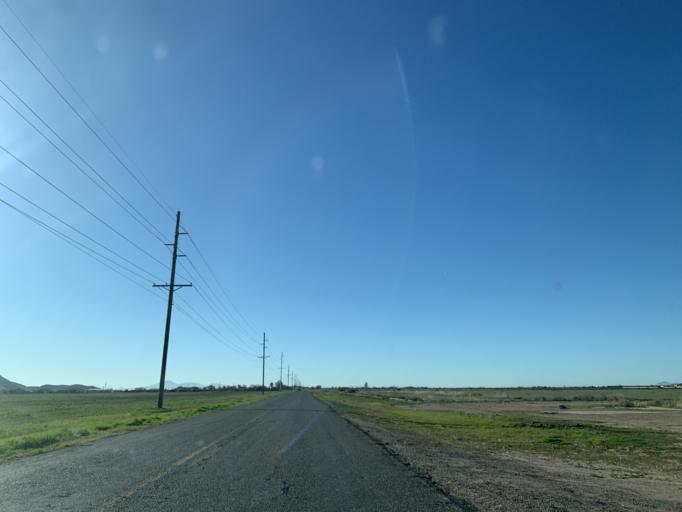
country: US
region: Arizona
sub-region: Pinal County
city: Casa Grande
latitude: 32.8503
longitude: -111.6725
